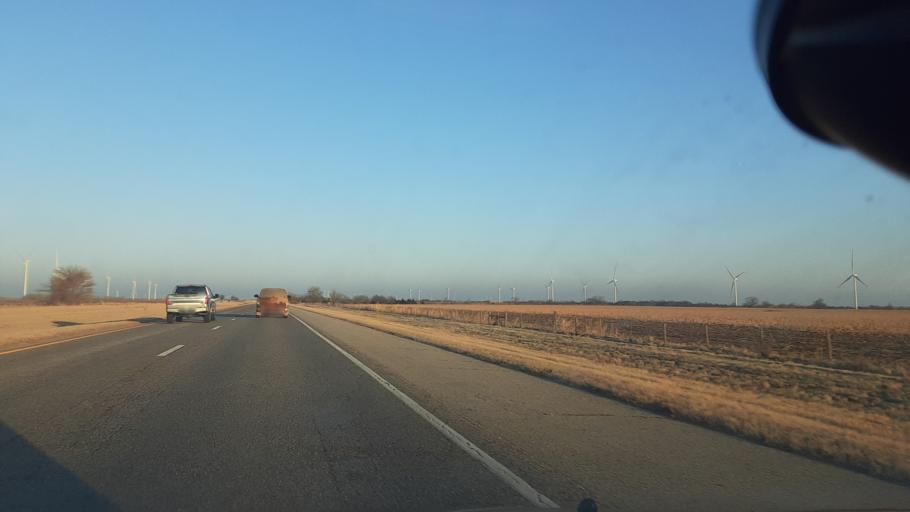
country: US
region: Oklahoma
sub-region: Noble County
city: Perry
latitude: 36.3975
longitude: -97.5294
